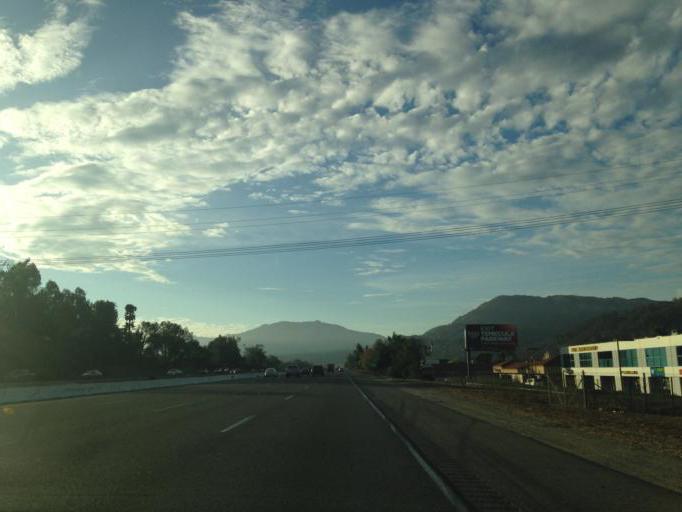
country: US
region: California
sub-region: Riverside County
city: Temecula
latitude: 33.4892
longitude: -117.1441
